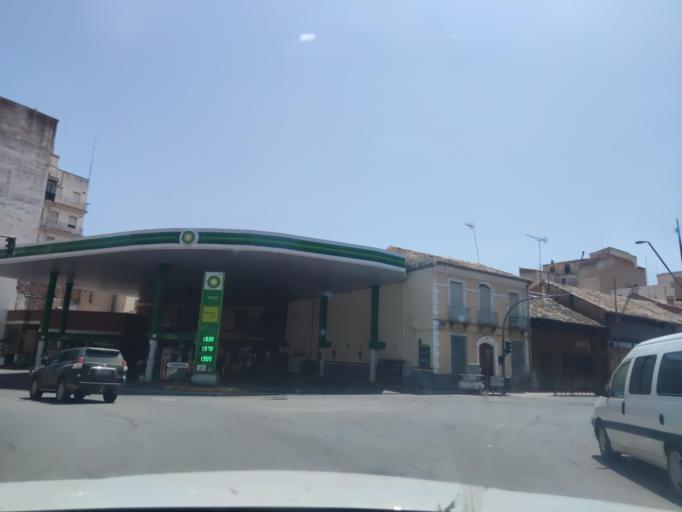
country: ES
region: Castille-La Mancha
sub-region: Provincia de Albacete
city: Hellin
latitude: 38.5116
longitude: -1.6972
